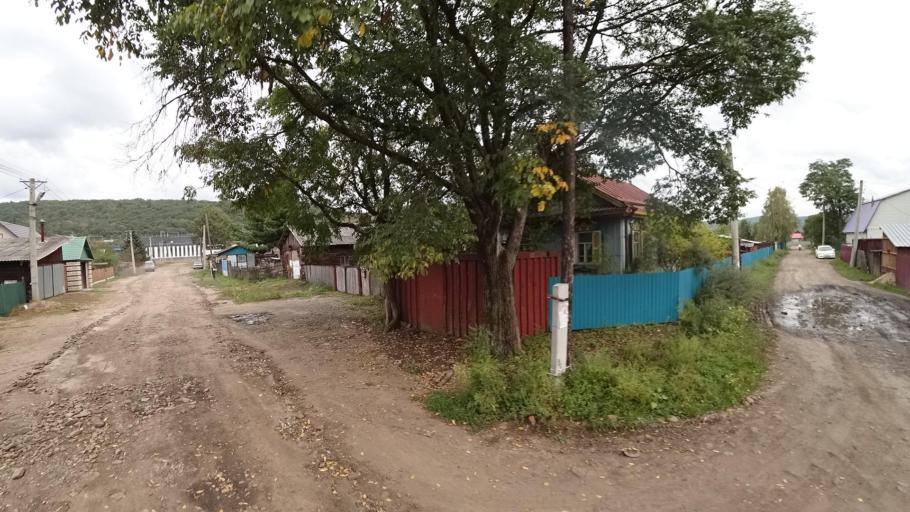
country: RU
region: Jewish Autonomous Oblast
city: Khingansk
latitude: 49.0028
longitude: 131.0504
